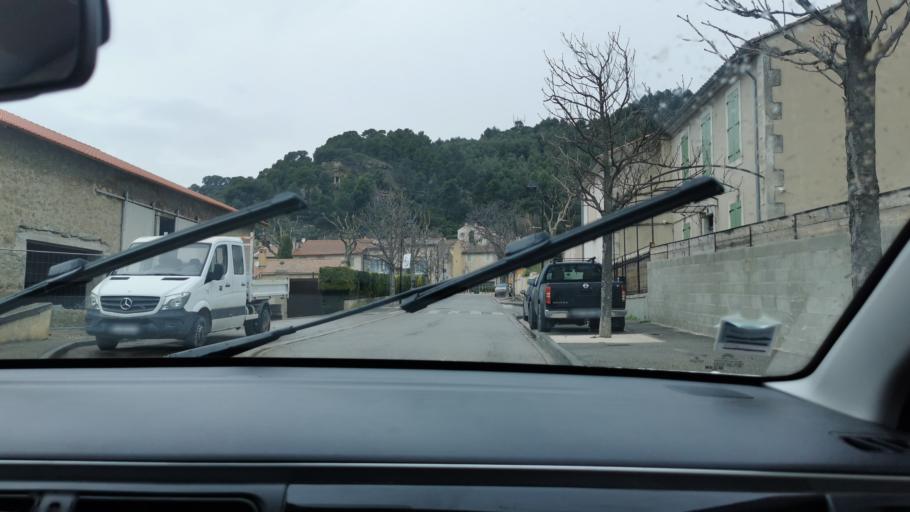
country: FR
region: Provence-Alpes-Cote d'Azur
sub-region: Departement des Bouches-du-Rhone
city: Lamanon
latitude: 43.7010
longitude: 5.0876
